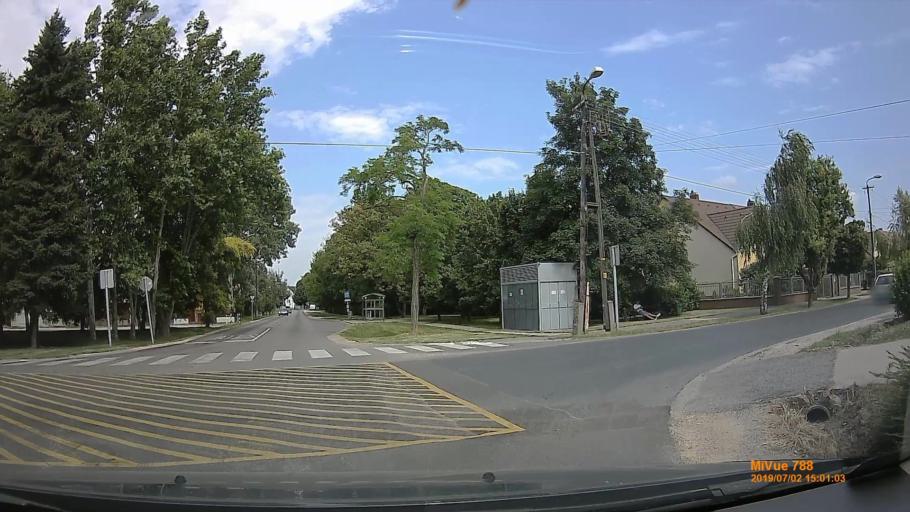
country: HU
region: Gyor-Moson-Sopron
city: Mosonmagyarovar
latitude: 47.8793
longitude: 17.2647
